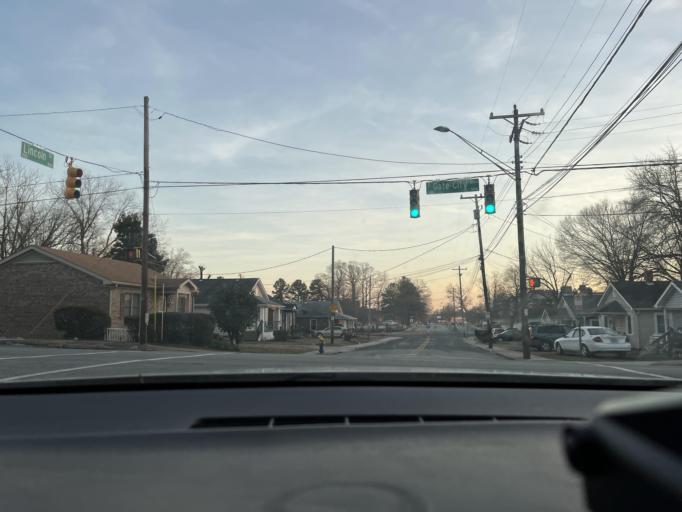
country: US
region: North Carolina
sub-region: Guilford County
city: Greensboro
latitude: 36.0631
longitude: -79.7651
